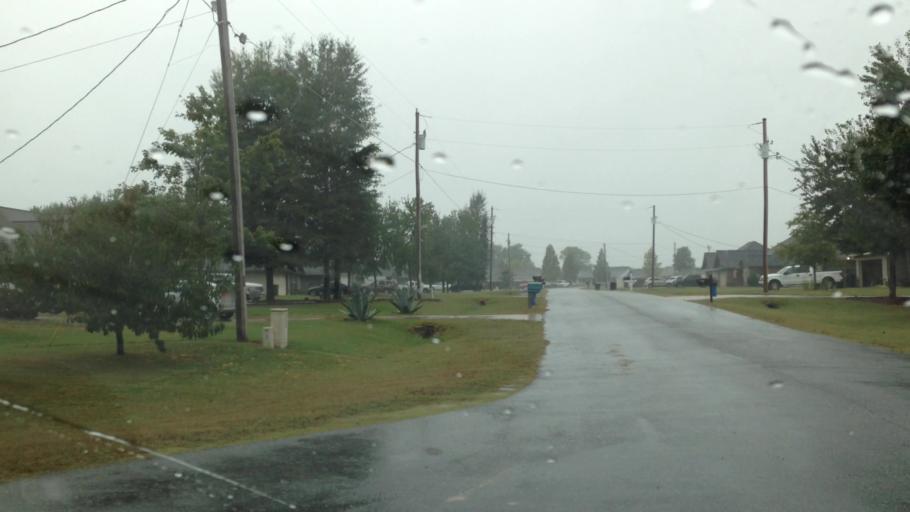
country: US
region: Georgia
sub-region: Muscogee County
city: Columbus
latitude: 32.2644
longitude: -84.9731
